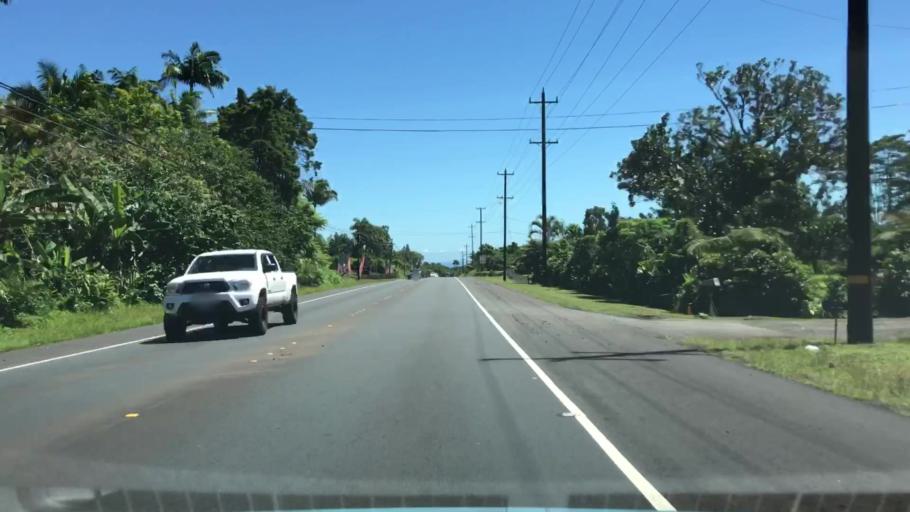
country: US
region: Hawaii
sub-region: Hawaii County
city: Mountain View
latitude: 19.5684
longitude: -155.0825
